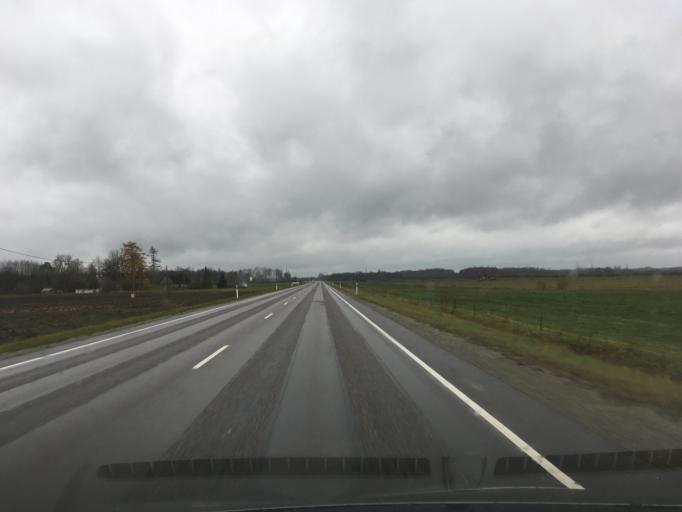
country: EE
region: Laeaene
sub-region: Lihula vald
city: Lihula
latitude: 58.7231
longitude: 23.9124
